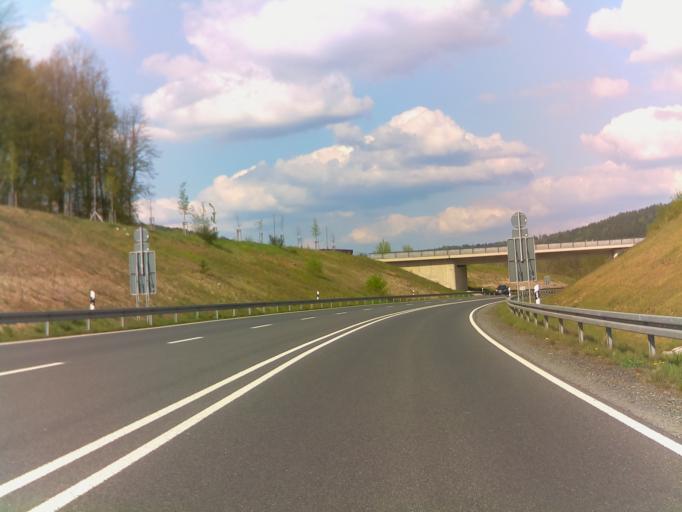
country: DE
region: Bavaria
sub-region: Upper Franconia
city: Rodental
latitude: 50.3036
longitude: 11.0120
